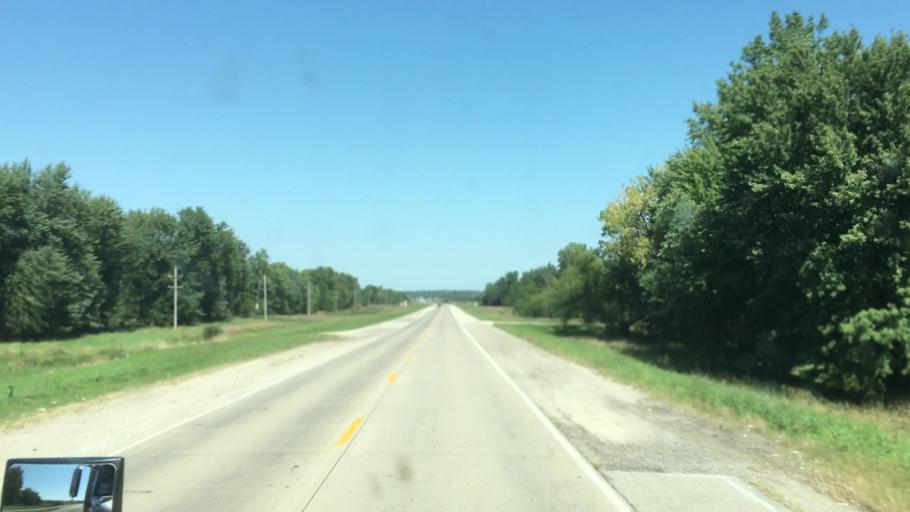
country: US
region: Iowa
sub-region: Benton County
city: Belle Plaine
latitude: 41.8607
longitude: -92.2779
